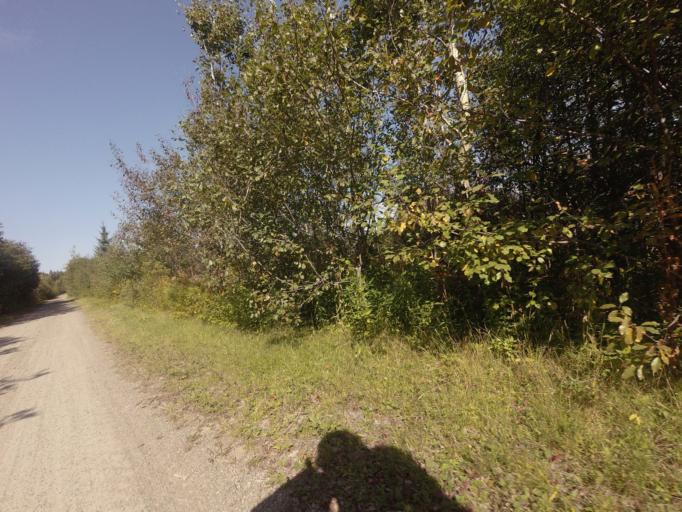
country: CA
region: Quebec
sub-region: Laurentides
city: Sainte-Agathe-des-Monts
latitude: 46.0658
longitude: -74.3099
